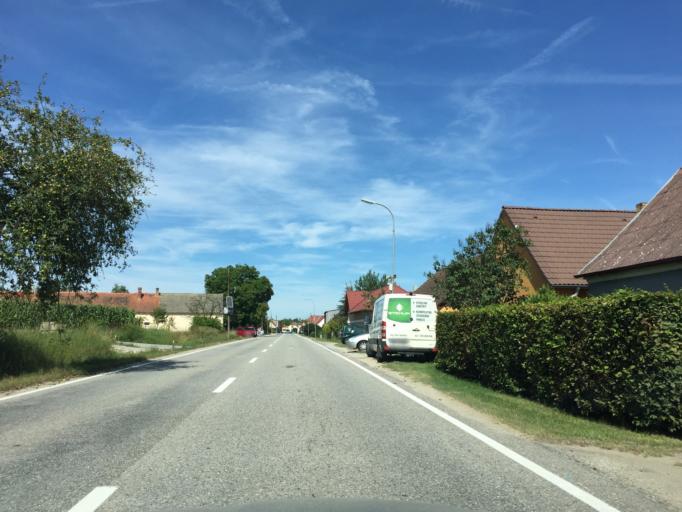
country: CZ
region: Jihocesky
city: Sevetin
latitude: 49.0862
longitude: 14.5426
